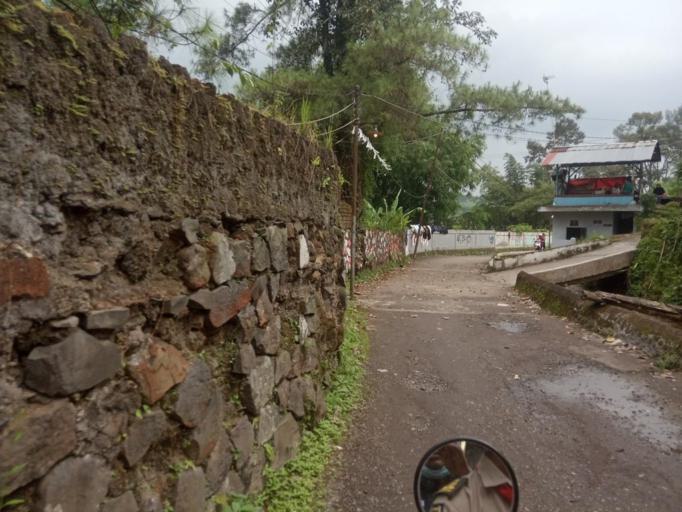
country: ID
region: West Java
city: Caringin
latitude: -6.6513
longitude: 106.8979
